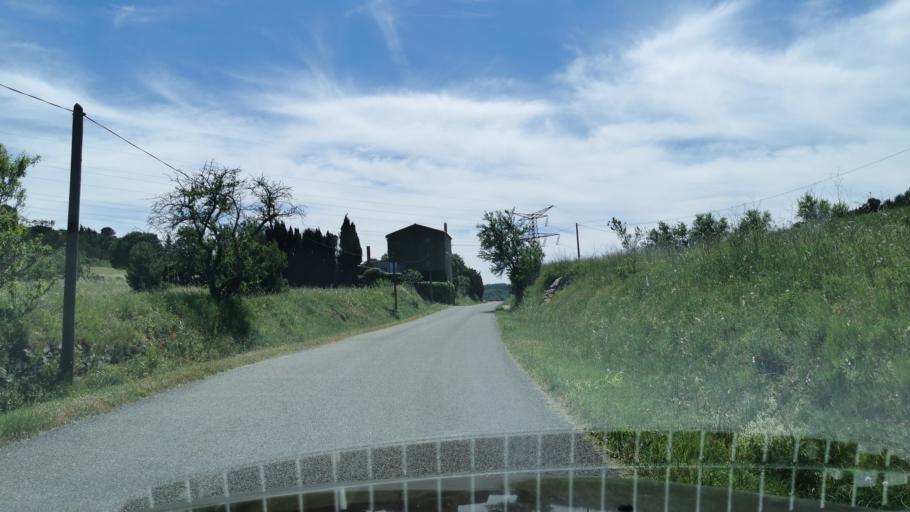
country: FR
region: Languedoc-Roussillon
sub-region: Departement de l'Aude
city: Nevian
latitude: 43.2022
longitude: 2.9032
